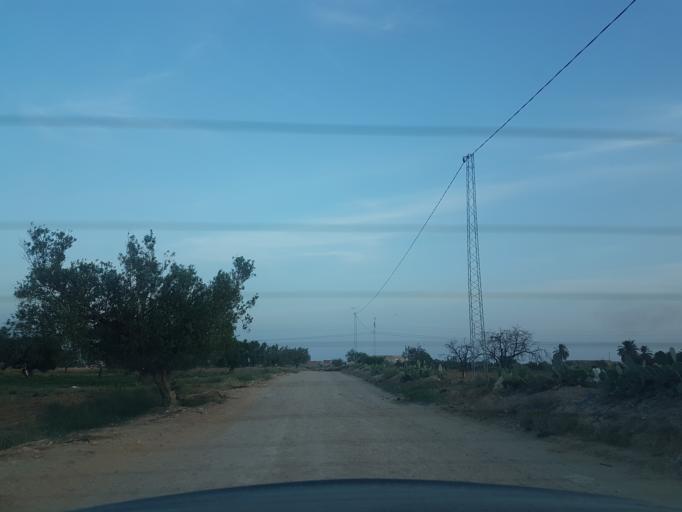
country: TN
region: Safaqis
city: Sfax
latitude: 34.7038
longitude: 10.6936
